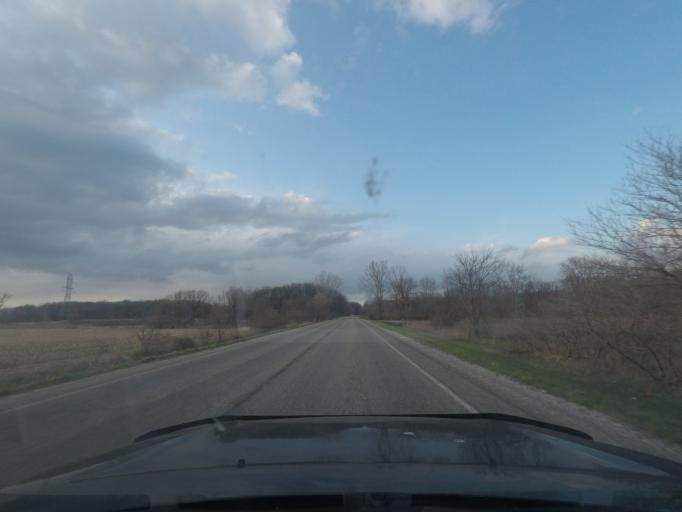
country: US
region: Indiana
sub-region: LaPorte County
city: LaPorte
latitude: 41.5496
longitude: -86.7399
